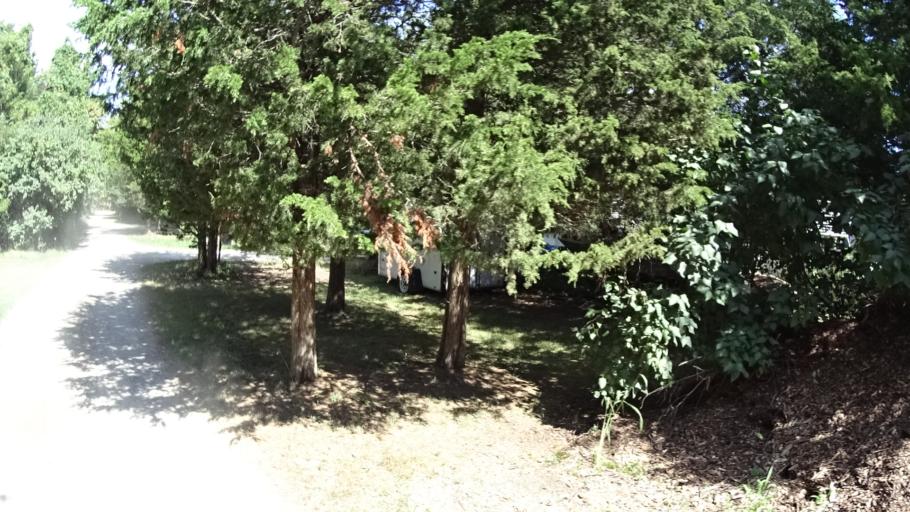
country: US
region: Ohio
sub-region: Erie County
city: Sandusky
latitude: 41.6046
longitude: -82.7150
